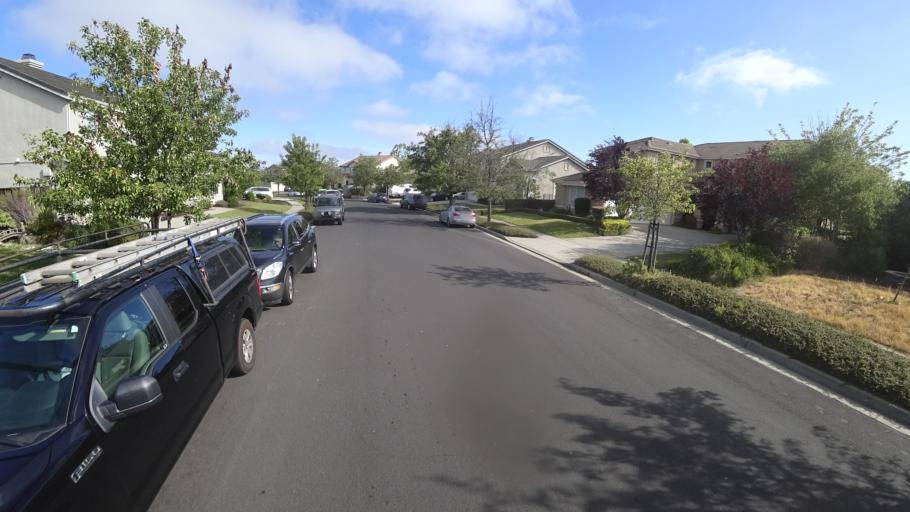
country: US
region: California
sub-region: Alameda County
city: Fairview
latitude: 37.6535
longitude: -122.0194
